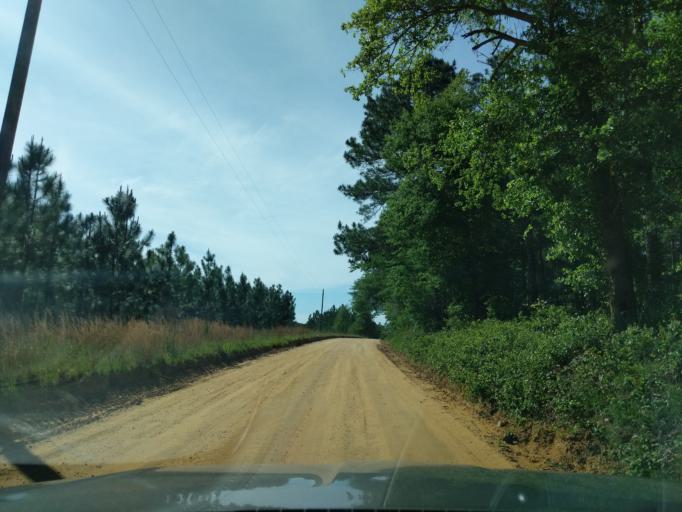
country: US
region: Georgia
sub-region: Jefferson County
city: Wrens
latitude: 33.2291
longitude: -82.3523
